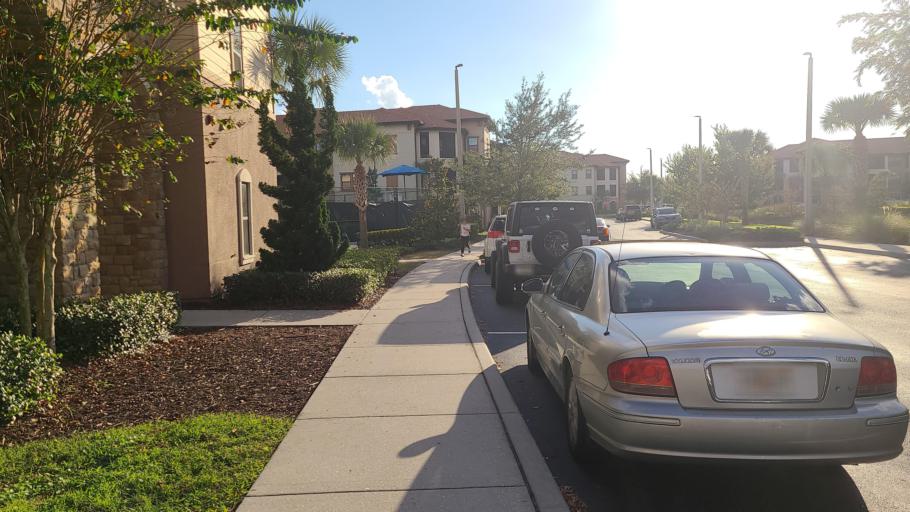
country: US
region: Florida
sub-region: Osceola County
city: Buenaventura Lakes
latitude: 28.3581
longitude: -81.2388
